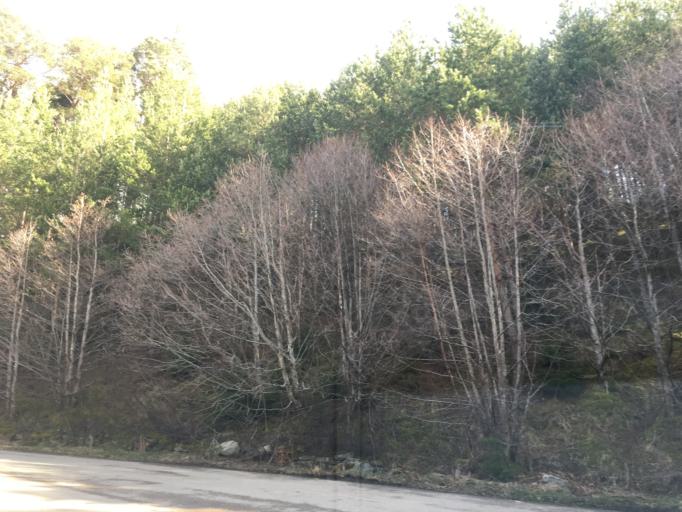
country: GB
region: Scotland
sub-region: Highland
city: Kingussie
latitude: 57.0705
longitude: -3.9976
